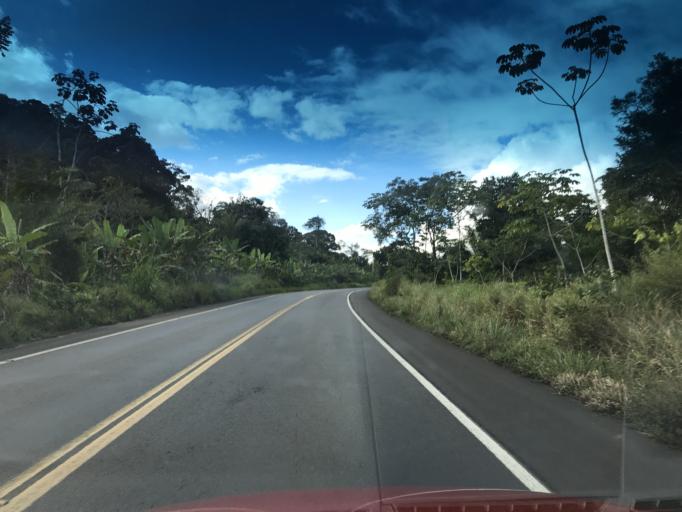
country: BR
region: Bahia
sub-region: Ibirapitanga
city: Ibirapitanga
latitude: -14.2018
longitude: -39.3150
